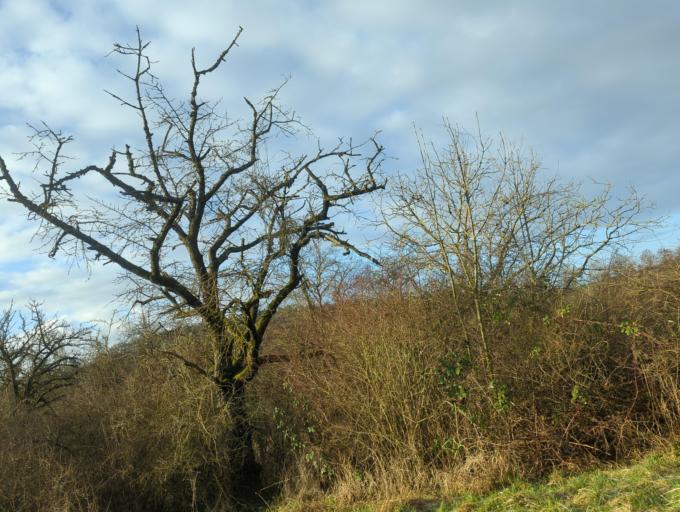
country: DE
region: Baden-Wuerttemberg
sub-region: Karlsruhe Region
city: Joehlingen
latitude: 49.0245
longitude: 8.5883
